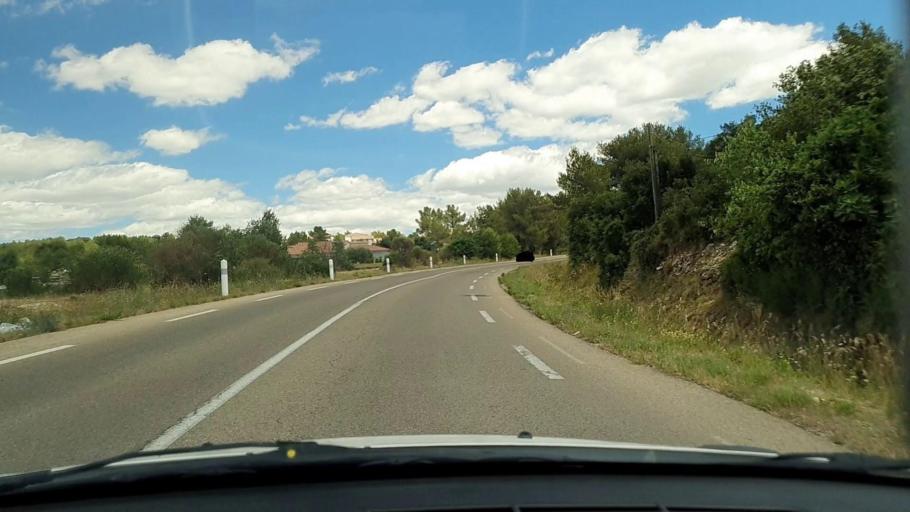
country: FR
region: Languedoc-Roussillon
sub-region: Departement du Gard
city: Poulx
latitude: 43.8713
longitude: 4.4088
